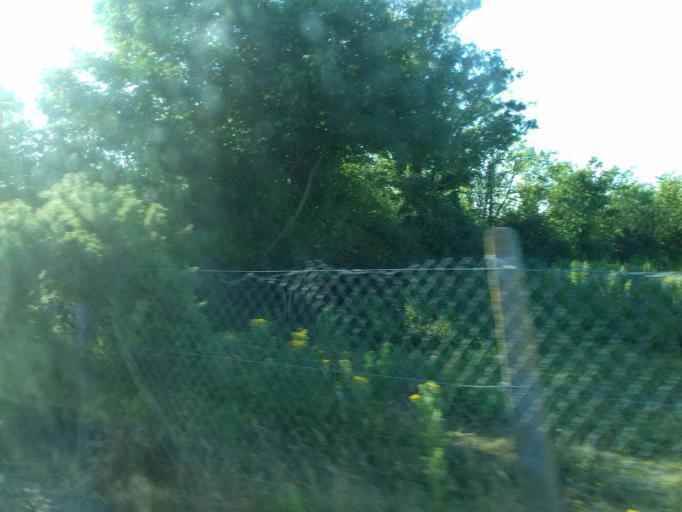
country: IE
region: Leinster
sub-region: Fingal County
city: Swords
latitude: 53.4924
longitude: -6.2999
